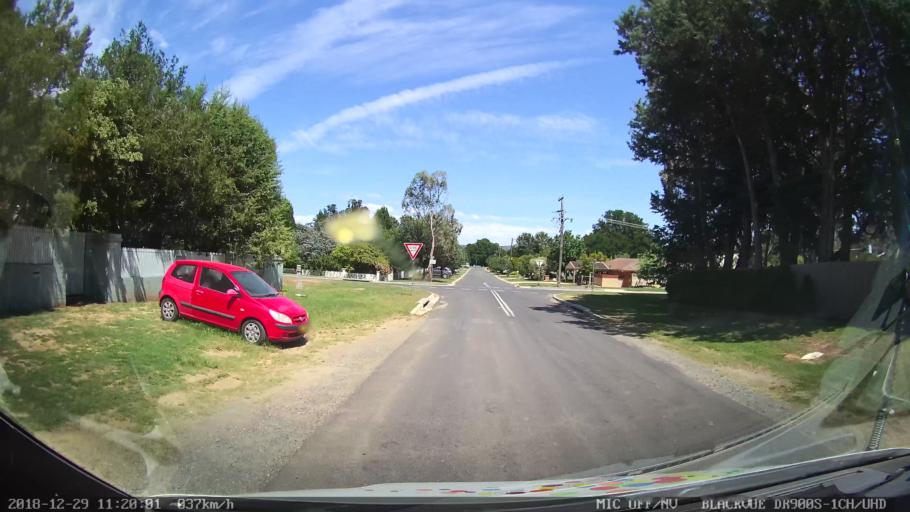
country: AU
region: New South Wales
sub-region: Palerang
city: Bungendore
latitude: -35.2584
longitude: 149.4404
